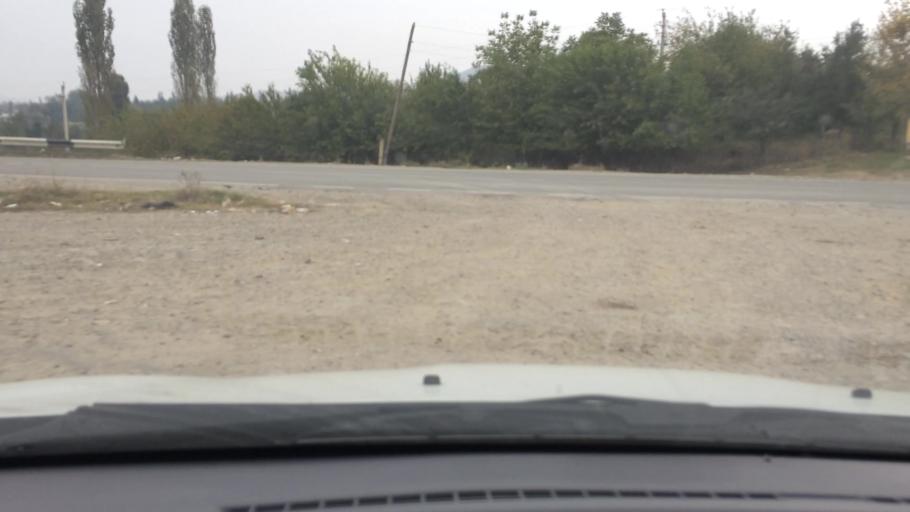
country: AM
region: Tavush
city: Bagratashen
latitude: 41.2322
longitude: 44.8167
